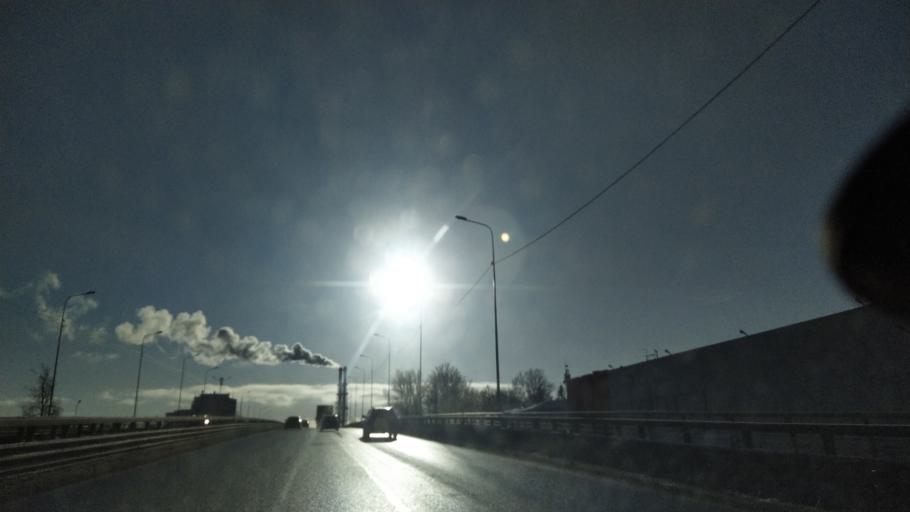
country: RU
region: Leningrad
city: Chernaya Rechka
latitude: 59.9948
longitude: 30.2997
